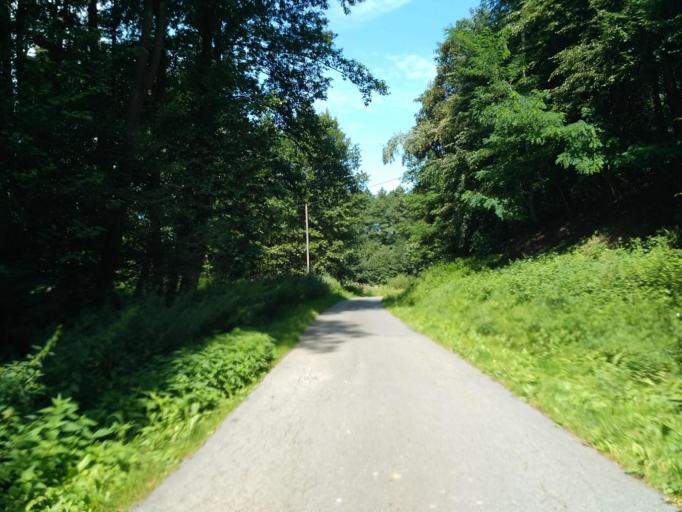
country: PL
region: Subcarpathian Voivodeship
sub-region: Powiat strzyzowski
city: Polomia
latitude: 49.9162
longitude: 21.8822
